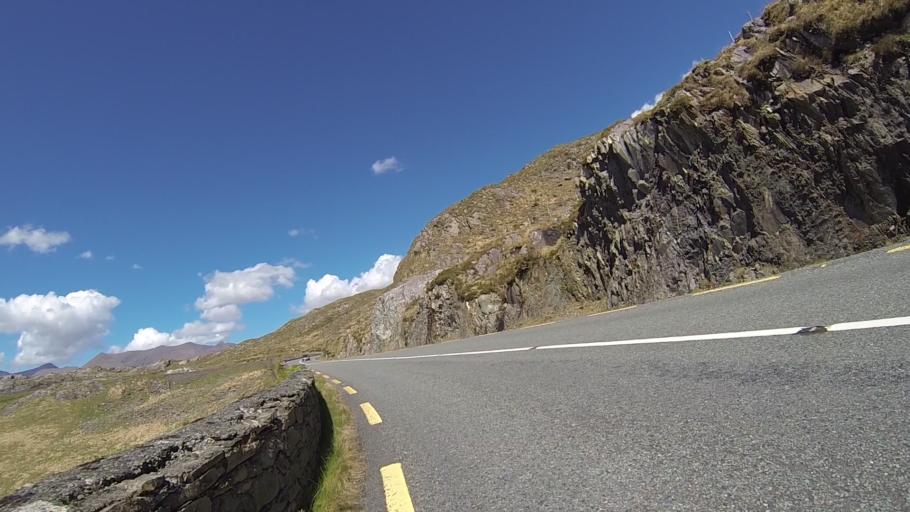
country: IE
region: Munster
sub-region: Ciarrai
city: Kenmare
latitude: 51.9364
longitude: -9.6528
